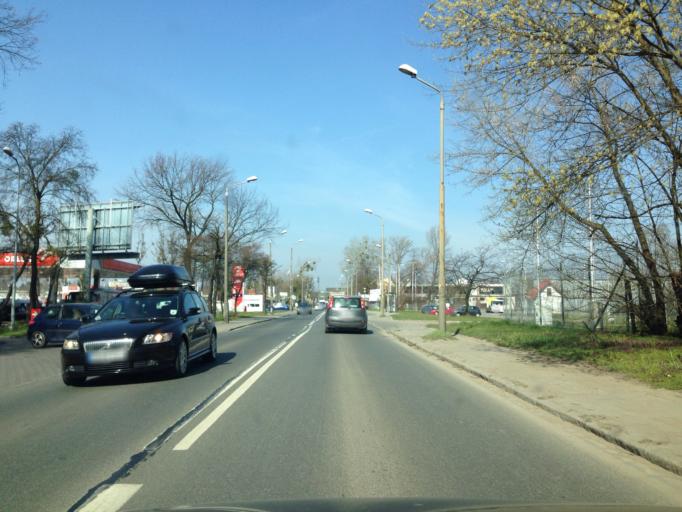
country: PL
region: Lower Silesian Voivodeship
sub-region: Powiat wroclawski
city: Wilczyce
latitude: 51.1137
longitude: 17.1183
